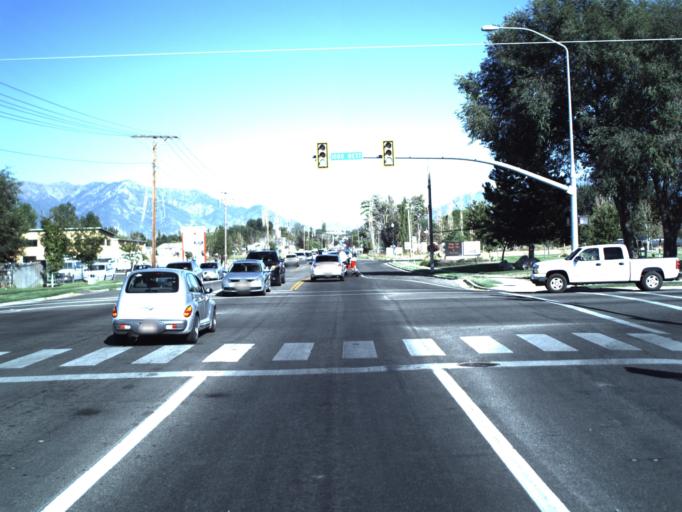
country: US
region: Utah
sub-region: Davis County
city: Clinton
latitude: 41.1399
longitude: -112.0456
